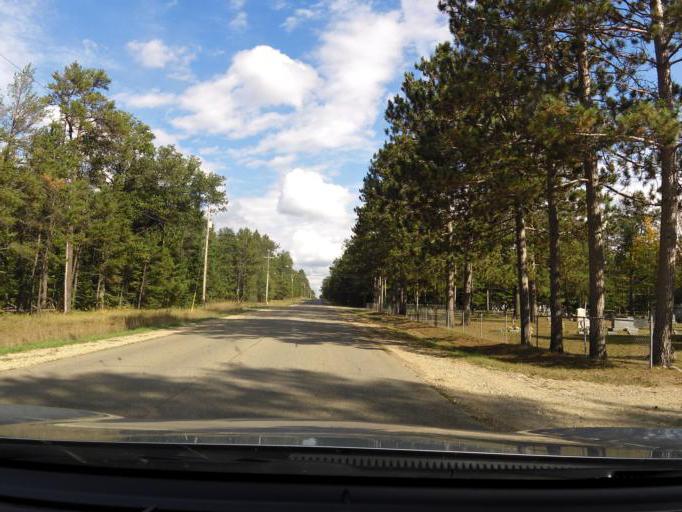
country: US
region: Michigan
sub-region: Roscommon County
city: Roscommon
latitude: 44.5257
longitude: -84.5820
